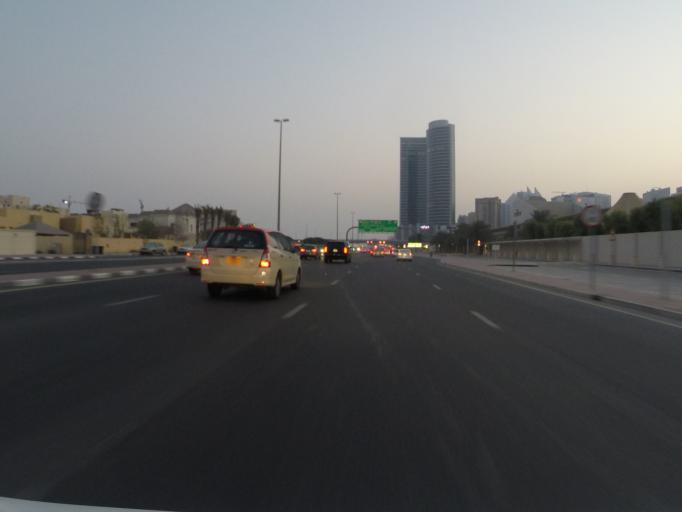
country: AE
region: Dubai
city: Dubai
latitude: 25.1006
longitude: 55.1847
